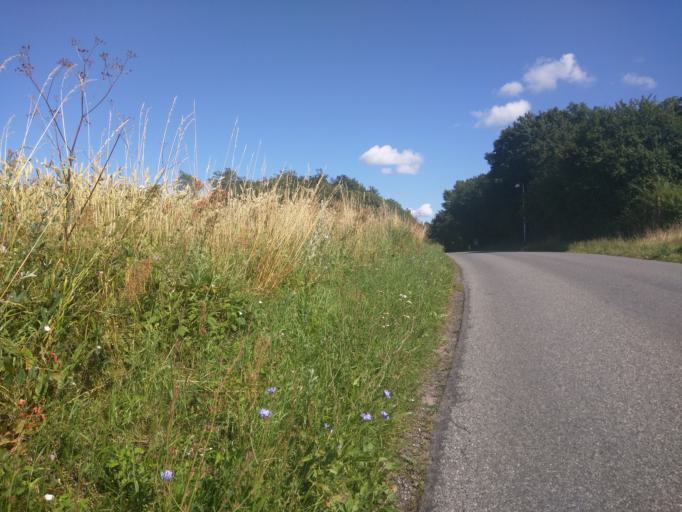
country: DK
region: Zealand
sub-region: Kalundborg Kommune
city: Svebolle
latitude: 55.6853
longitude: 11.3029
